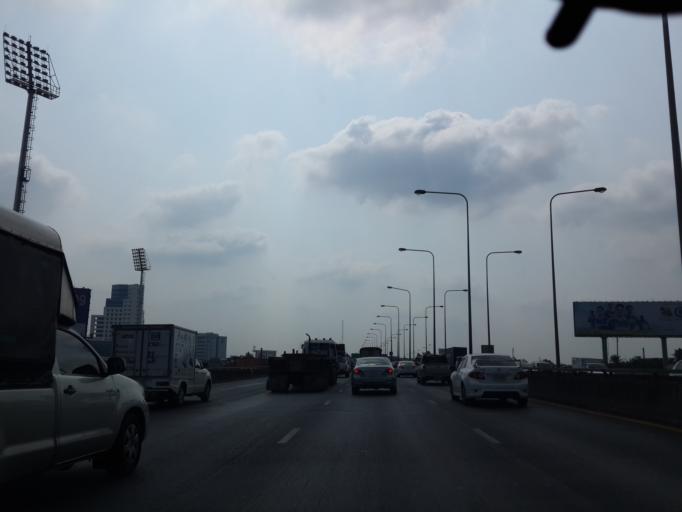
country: TH
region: Bangkok
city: Khlong Toei
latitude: 13.7151
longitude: 100.5584
